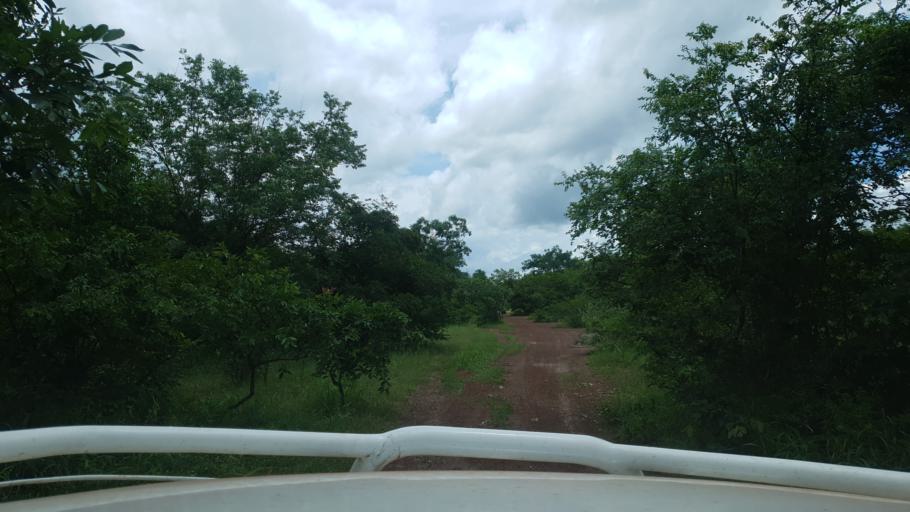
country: ML
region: Koulikoro
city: Banamba
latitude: 13.1960
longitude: -7.3235
